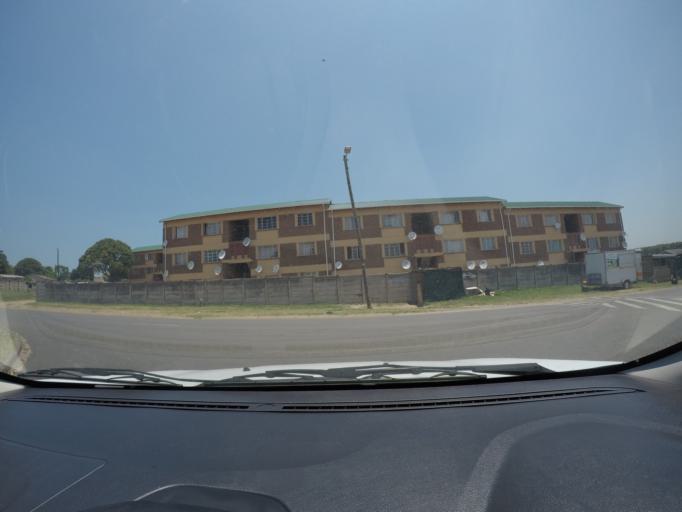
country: ZA
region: KwaZulu-Natal
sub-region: uThungulu District Municipality
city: eSikhawini
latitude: -28.8822
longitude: 31.8901
